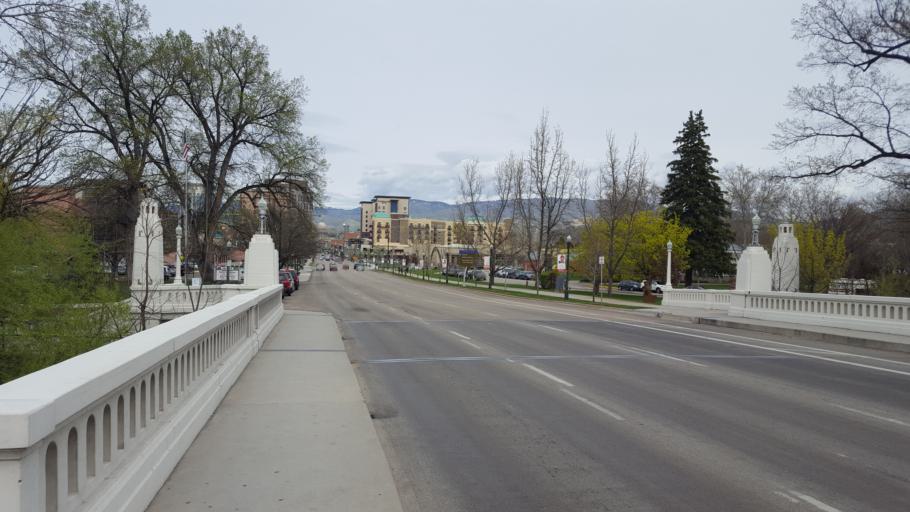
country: US
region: Idaho
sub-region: Ada County
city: Boise
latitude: 43.6114
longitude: -116.2047
